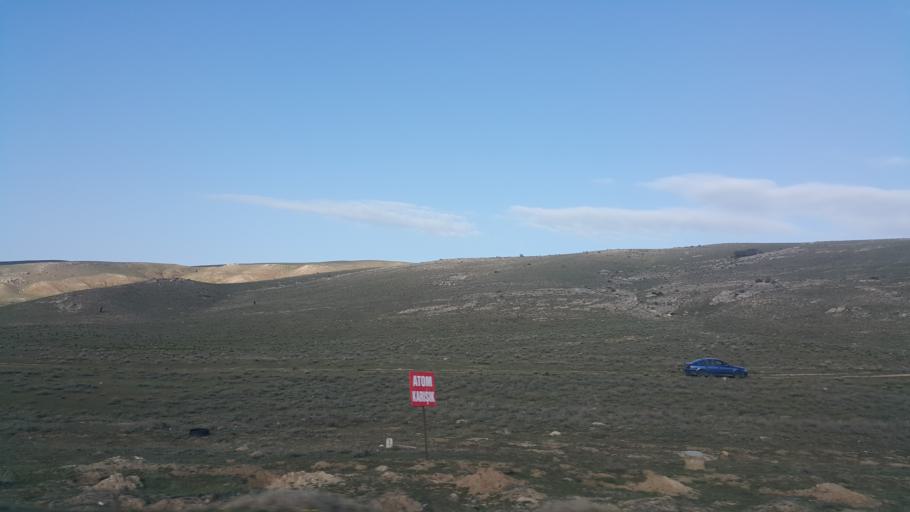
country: TR
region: Konya
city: Kulu
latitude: 39.1284
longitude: 33.3447
